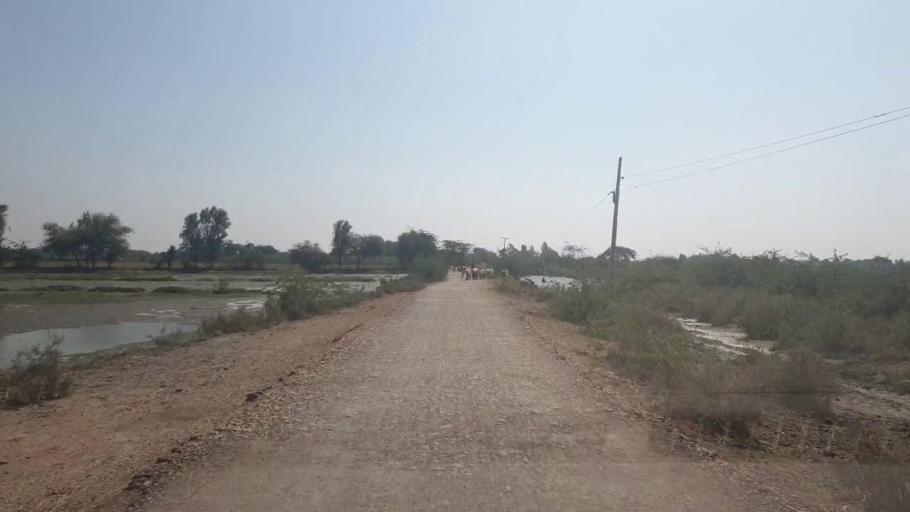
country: PK
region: Sindh
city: Badin
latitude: 24.6349
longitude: 68.9122
